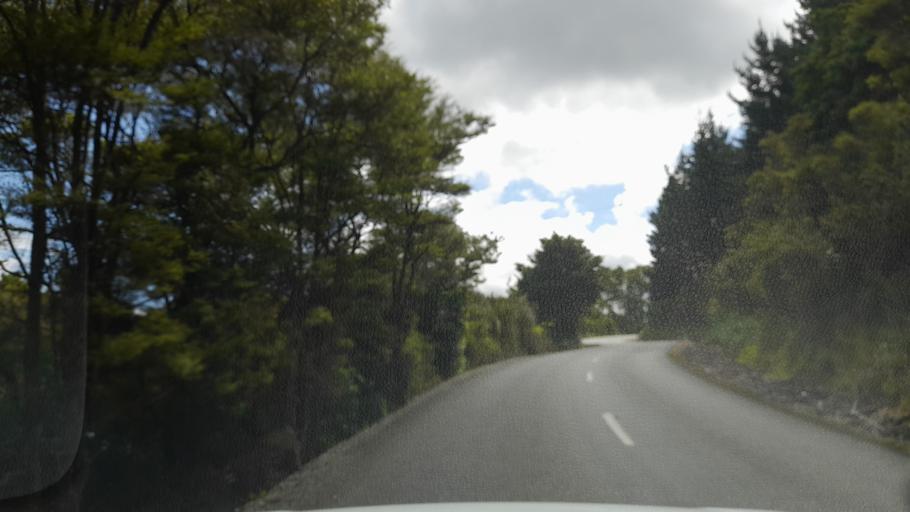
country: NZ
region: Northland
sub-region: Whangarei
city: Maungatapere
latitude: -35.6915
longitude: 174.0419
